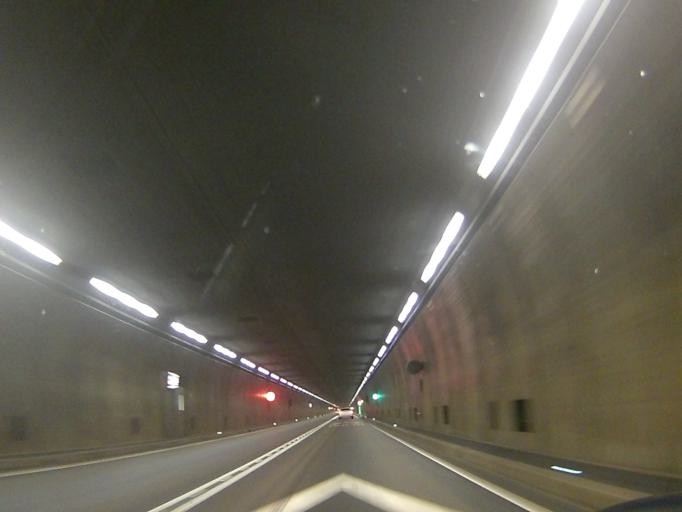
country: CH
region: Uri
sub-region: Uri
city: Andermatt
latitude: 46.6091
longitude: 8.5678
